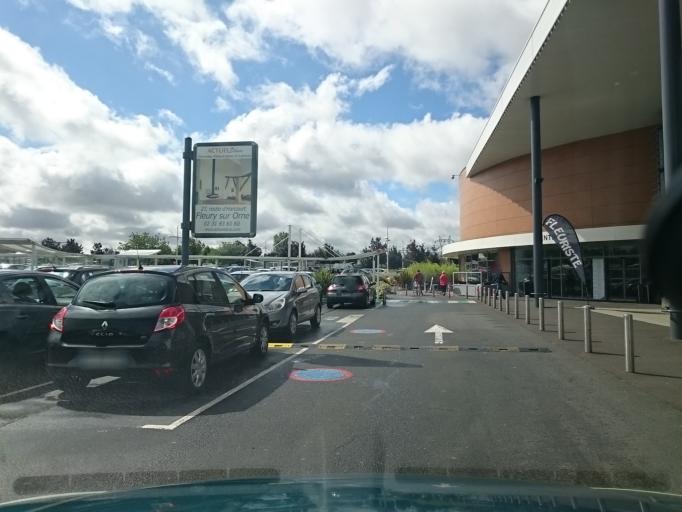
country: FR
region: Lower Normandy
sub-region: Departement du Calvados
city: Ifs
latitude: 49.1413
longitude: -0.3384
